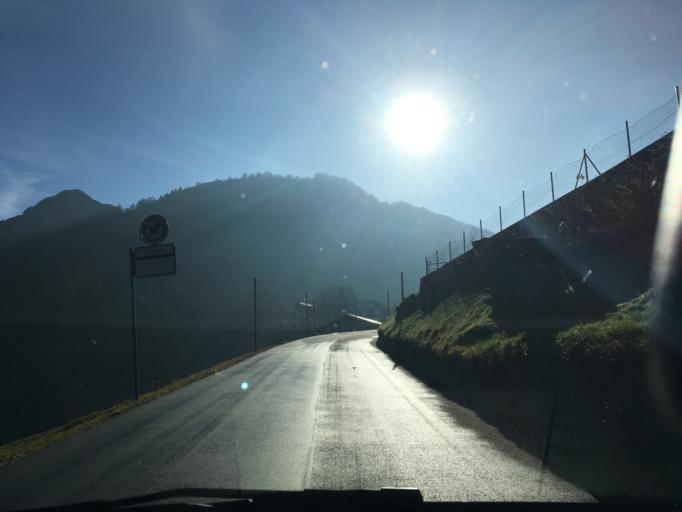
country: CH
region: Ticino
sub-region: Locarno District
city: Magadino
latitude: 46.1121
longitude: 8.8451
